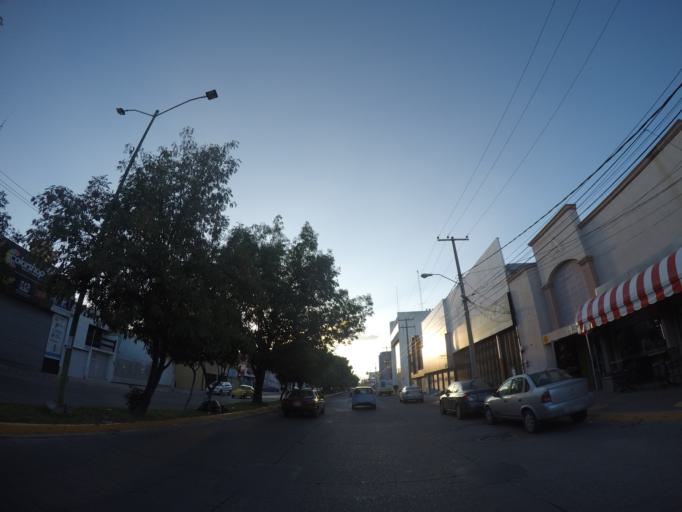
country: MX
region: San Luis Potosi
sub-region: San Luis Potosi
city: San Luis Potosi
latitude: 22.1418
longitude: -100.9969
